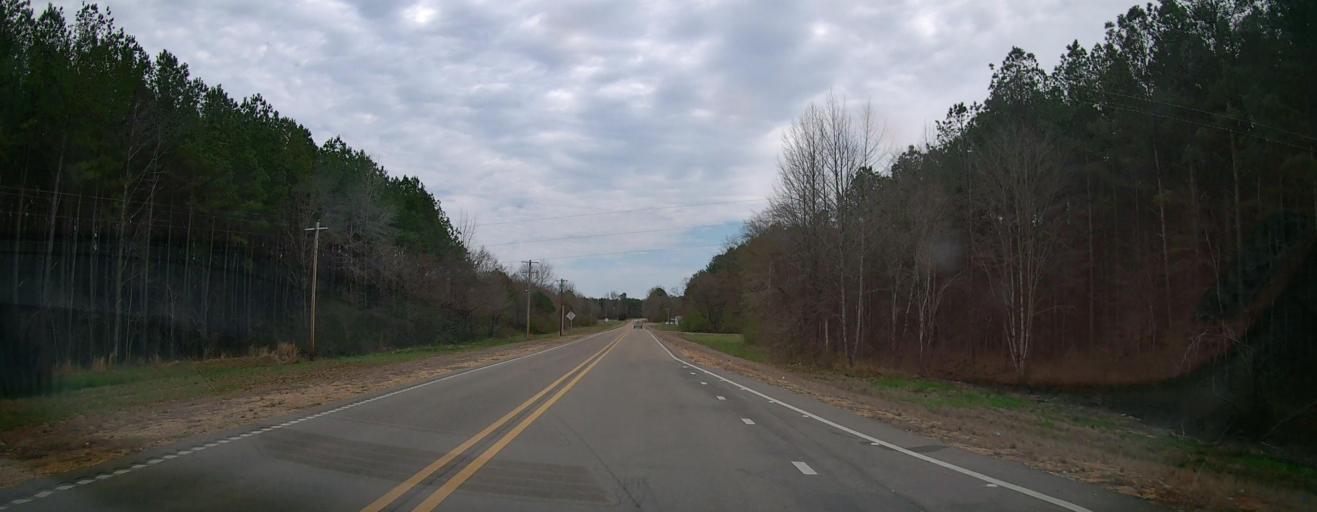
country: US
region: Mississippi
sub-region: Itawamba County
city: Fulton
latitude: 34.2316
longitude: -88.2471
